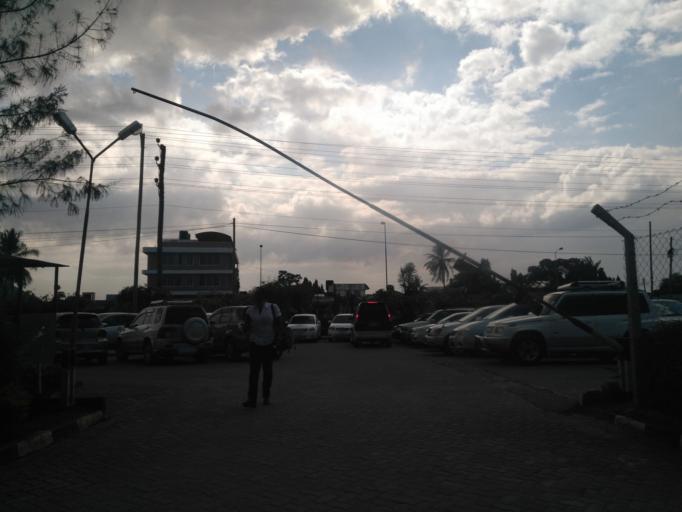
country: TZ
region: Dar es Salaam
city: Magomeni
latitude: -6.7838
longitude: 39.2642
